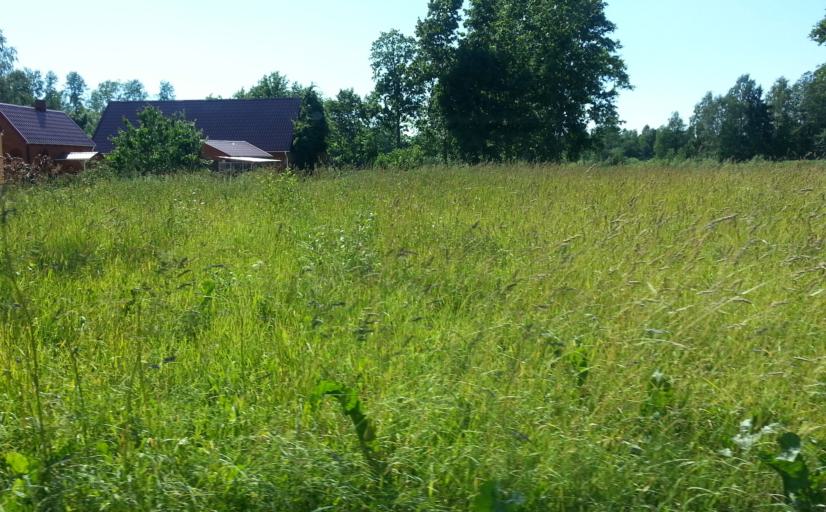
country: LT
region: Panevezys
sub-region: Birzai
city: Birzai
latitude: 56.2439
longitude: 24.6927
